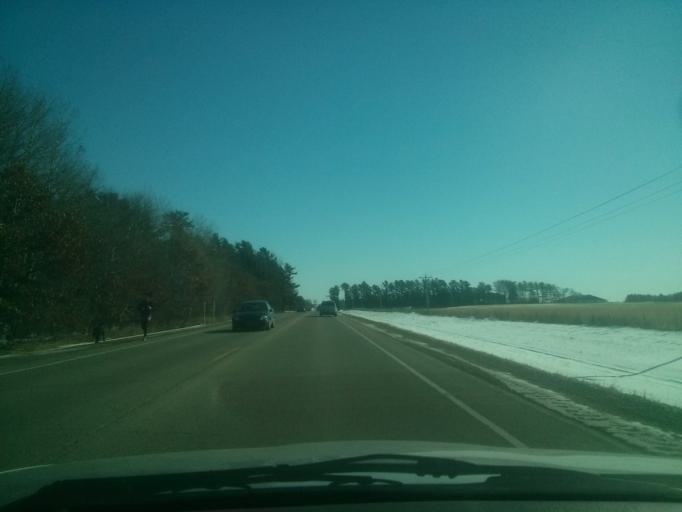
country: US
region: Wisconsin
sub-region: Saint Croix County
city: New Richmond
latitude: 45.1367
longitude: -92.4034
